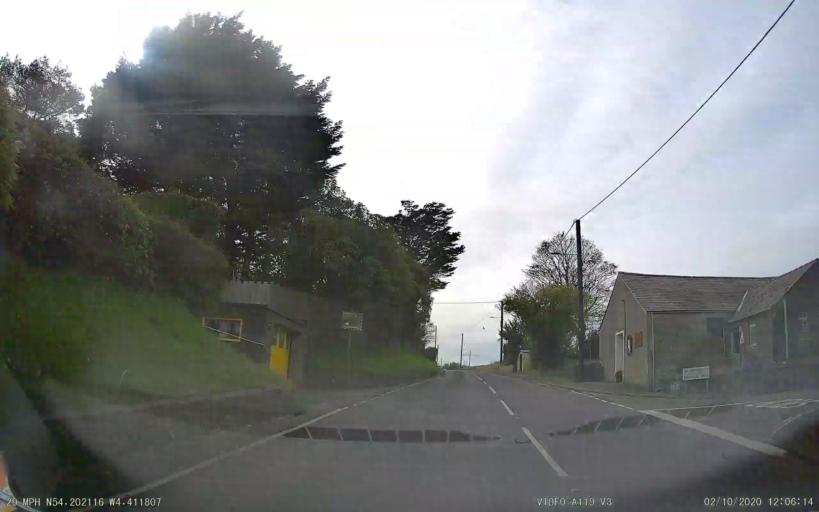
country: IM
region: Laxey
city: Laxey
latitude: 54.2021
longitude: -4.4118
